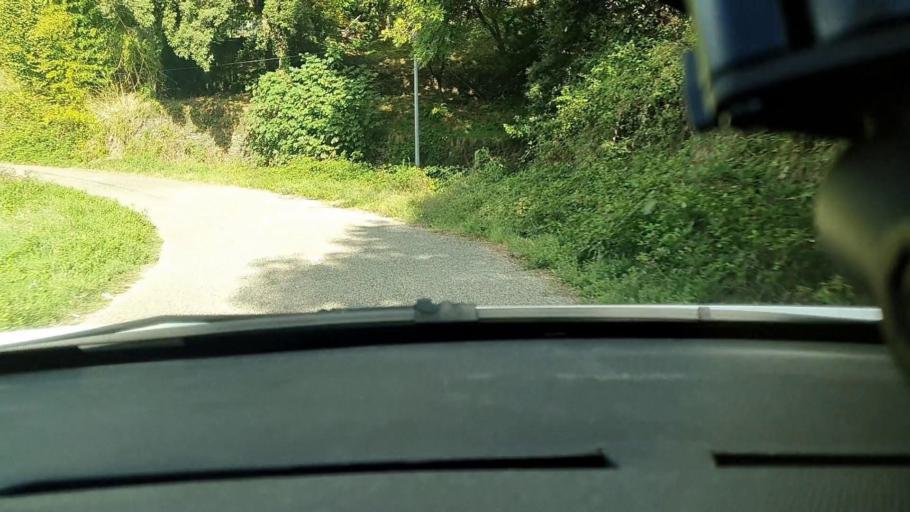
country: FR
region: Languedoc-Roussillon
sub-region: Departement du Gard
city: Besseges
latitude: 44.3340
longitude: 3.9976
